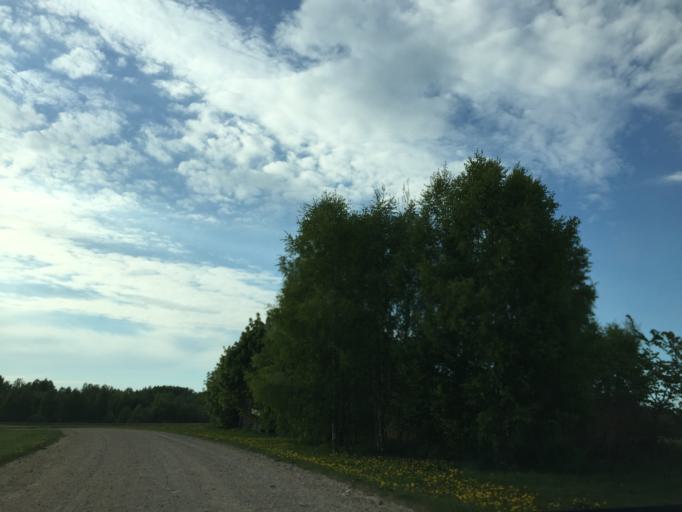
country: LV
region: Limbazu Rajons
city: Limbazi
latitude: 57.3727
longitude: 24.6885
